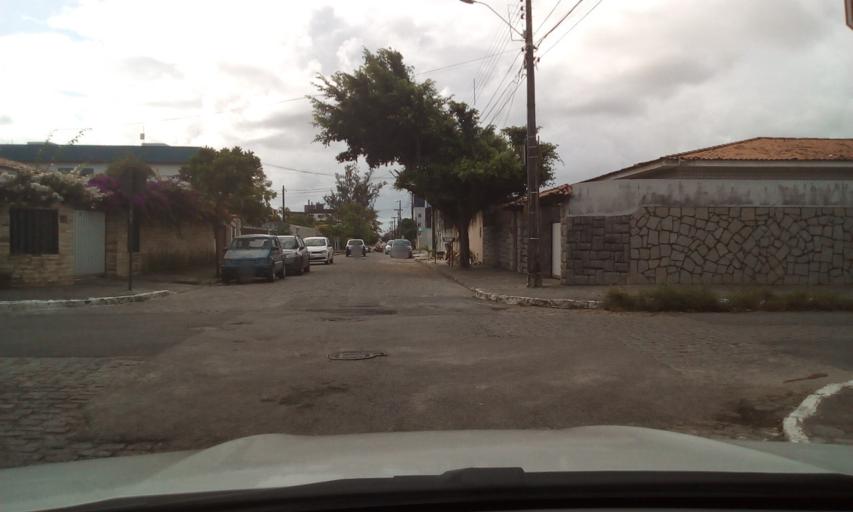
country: BR
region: Paraiba
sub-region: Joao Pessoa
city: Joao Pessoa
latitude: -7.1600
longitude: -34.8745
